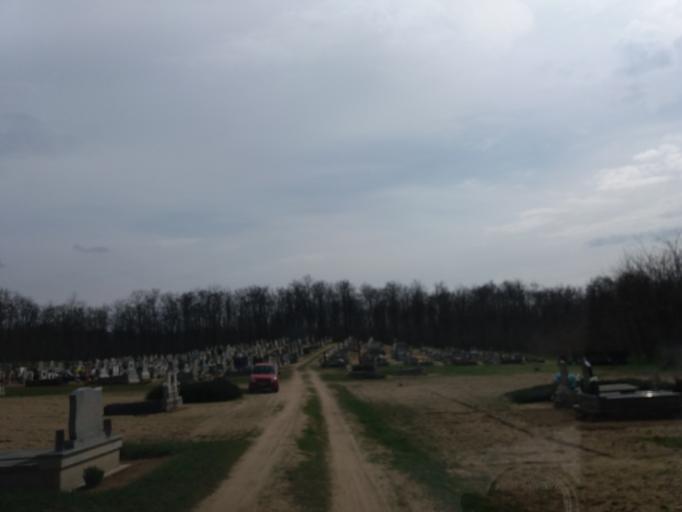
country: HU
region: Szabolcs-Szatmar-Bereg
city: Petnehaza
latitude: 48.0512
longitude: 22.0452
